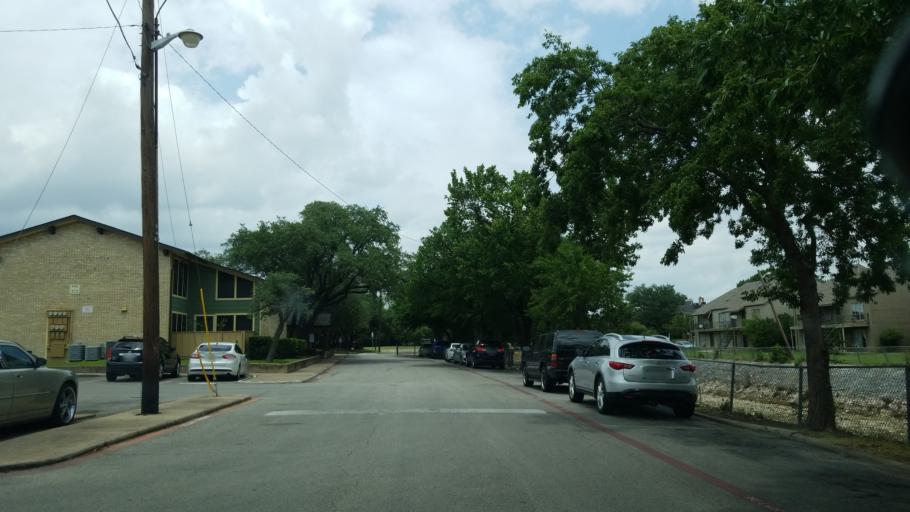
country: US
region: Texas
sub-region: Dallas County
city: Farmers Branch
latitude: 32.8736
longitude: -96.8664
